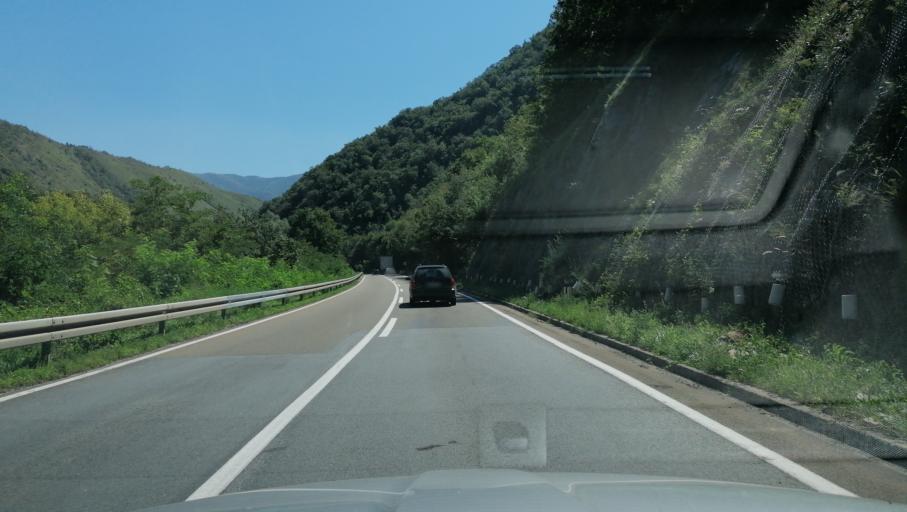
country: RS
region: Central Serbia
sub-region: Raski Okrug
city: Kraljevo
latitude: 43.5702
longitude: 20.5938
